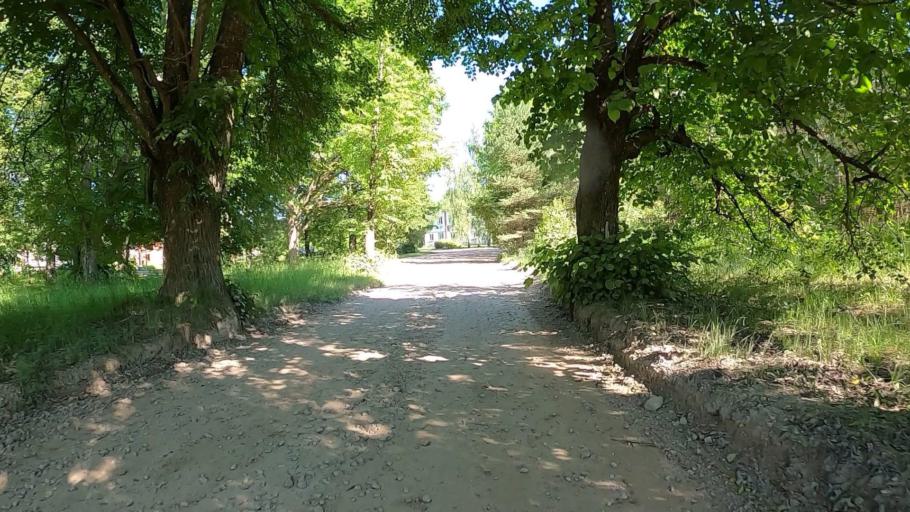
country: LV
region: Stopini
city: Ulbroka
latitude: 56.9122
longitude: 24.3116
